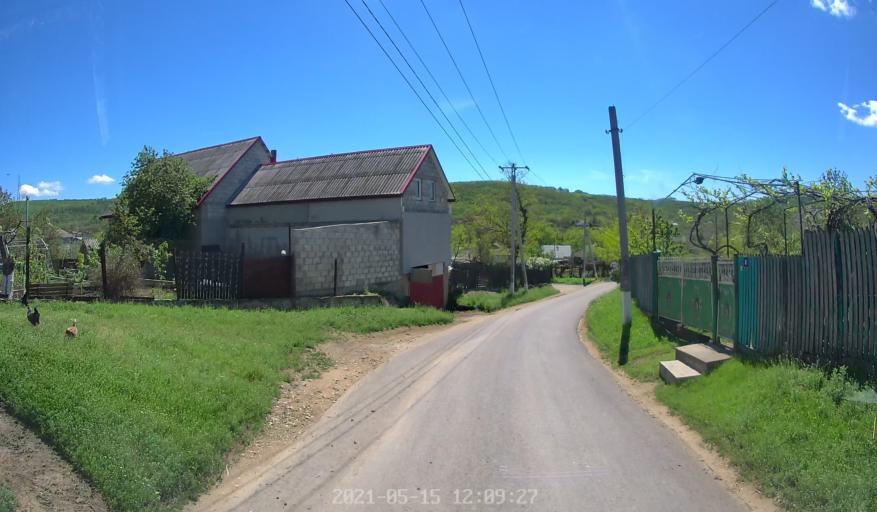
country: MD
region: Hincesti
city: Hincesti
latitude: 46.7994
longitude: 28.5414
